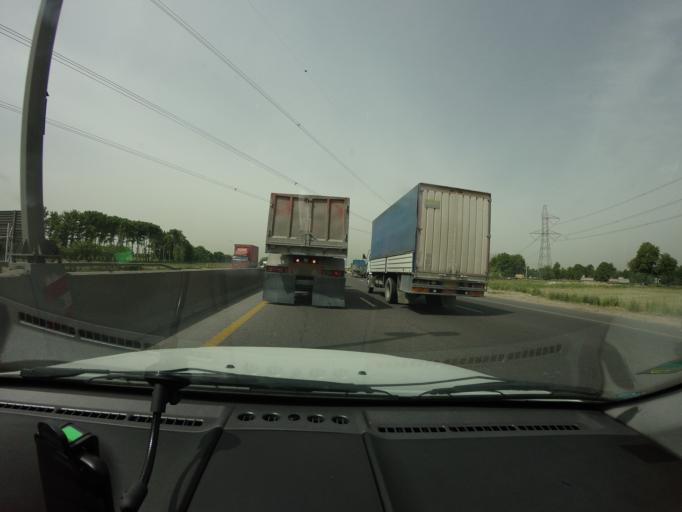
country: IR
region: Tehran
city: Eslamshahr
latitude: 35.6180
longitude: 51.2194
